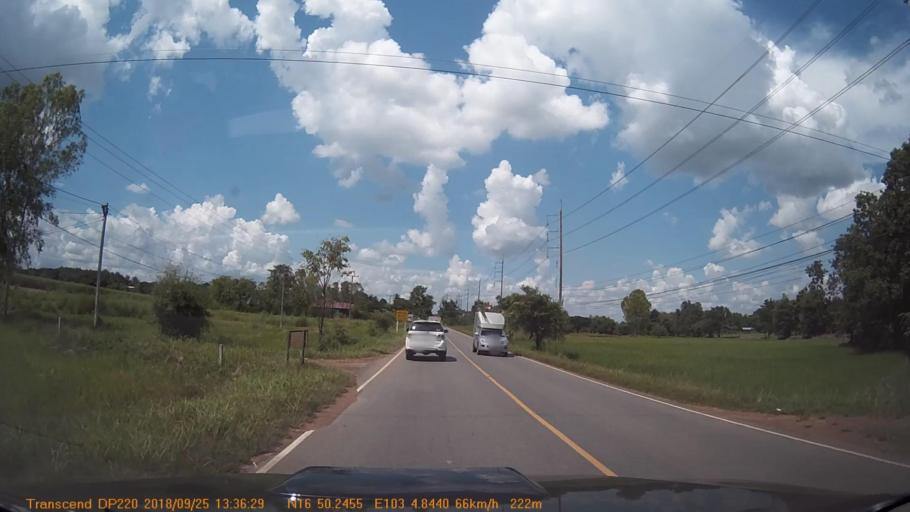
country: TH
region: Khon Kaen
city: Kranuan
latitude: 16.8375
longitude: 103.0807
